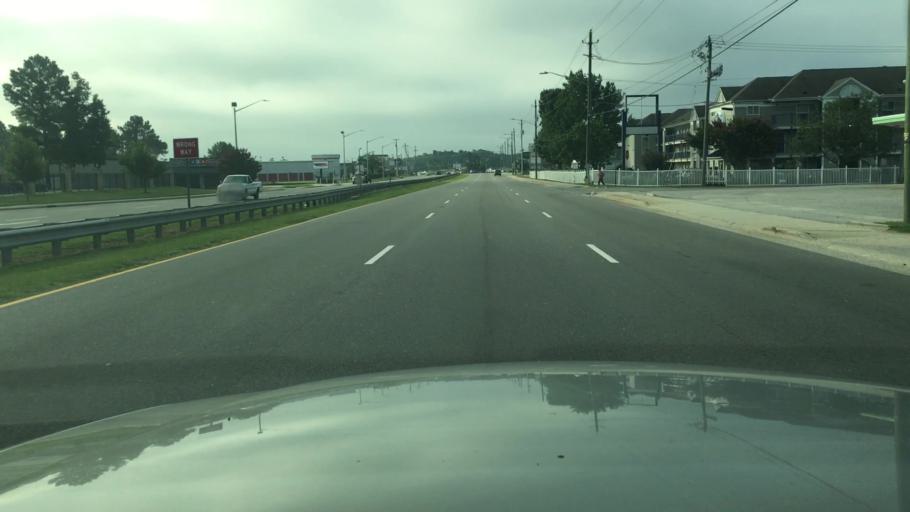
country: US
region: North Carolina
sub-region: Cumberland County
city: Fayetteville
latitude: 35.0808
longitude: -78.9431
